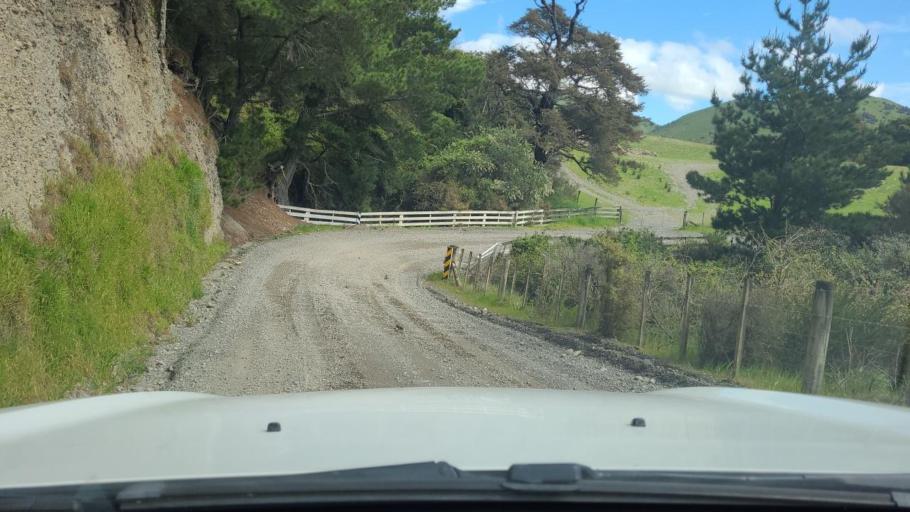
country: NZ
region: Wellington
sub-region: South Wairarapa District
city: Waipawa
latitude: -41.3208
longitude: 175.4125
